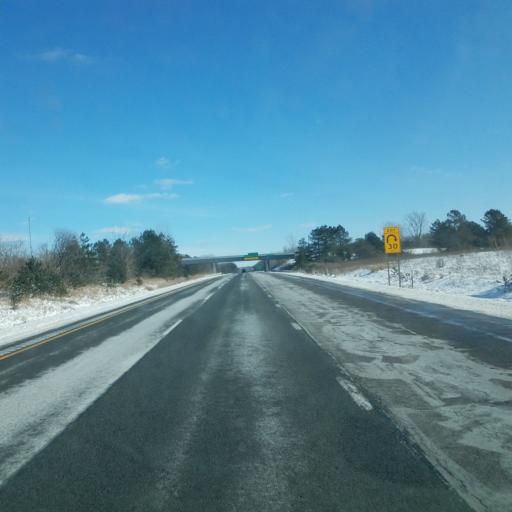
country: US
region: Michigan
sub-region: Ingham County
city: Williamston
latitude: 42.6653
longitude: -84.2845
